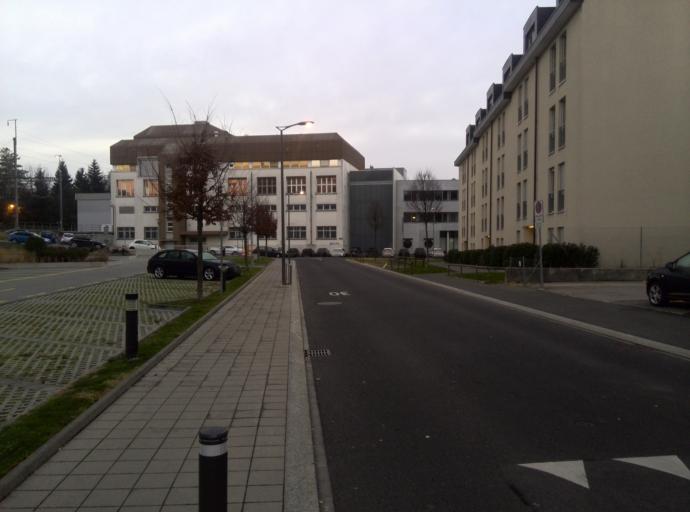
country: CH
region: Vaud
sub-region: Morges District
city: Morges
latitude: 46.5124
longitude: 6.4972
